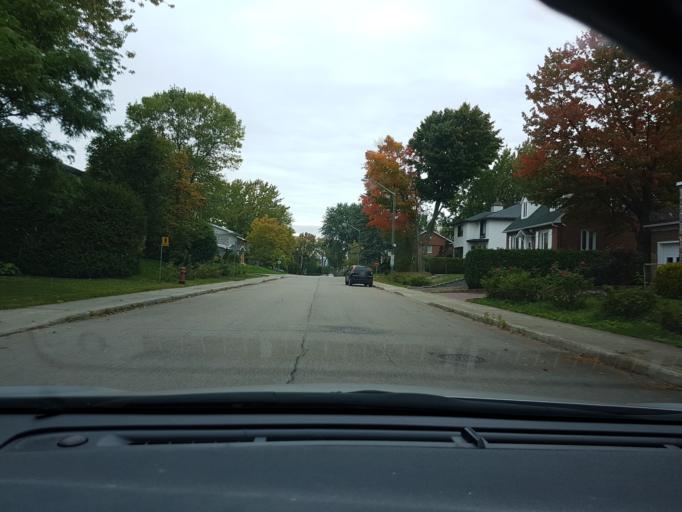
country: CA
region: Quebec
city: Quebec
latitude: 46.7884
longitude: -71.2648
